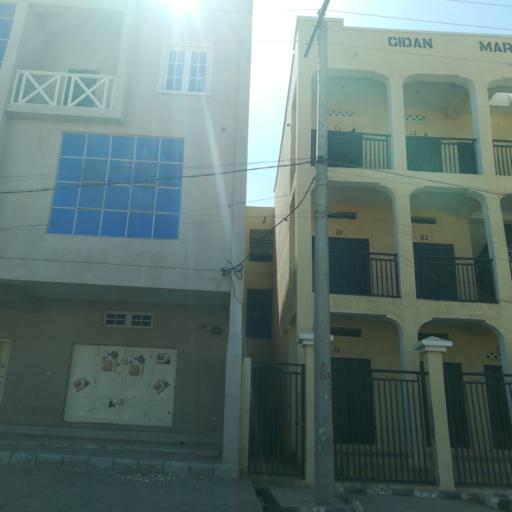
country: NG
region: Kano
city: Kano
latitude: 11.9985
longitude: 8.5287
